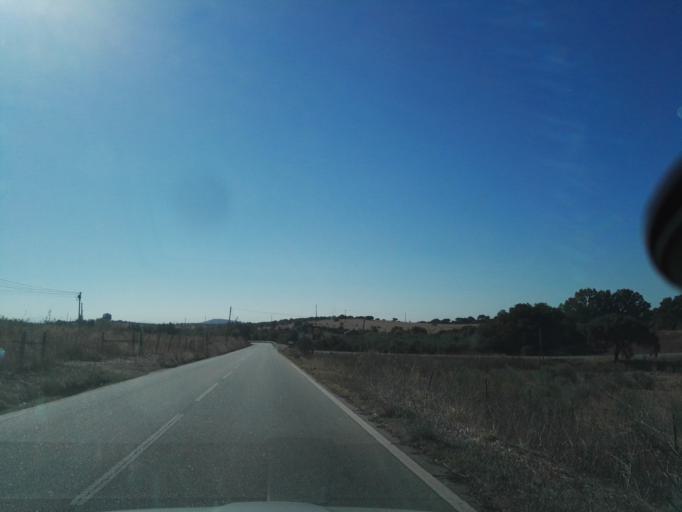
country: PT
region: Portalegre
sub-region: Elvas
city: Elvas
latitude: 38.9037
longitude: -7.1792
